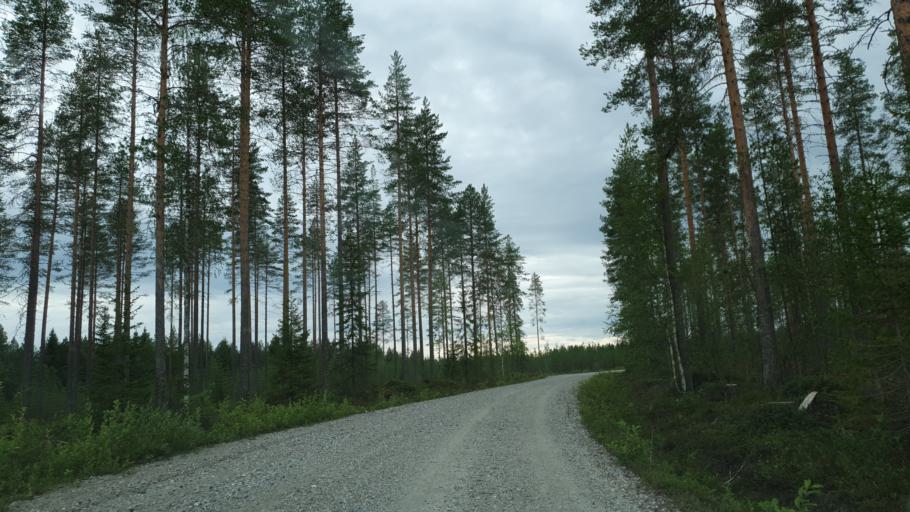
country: FI
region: Kainuu
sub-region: Kehys-Kainuu
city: Kuhmo
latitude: 64.4372
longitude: 29.5667
